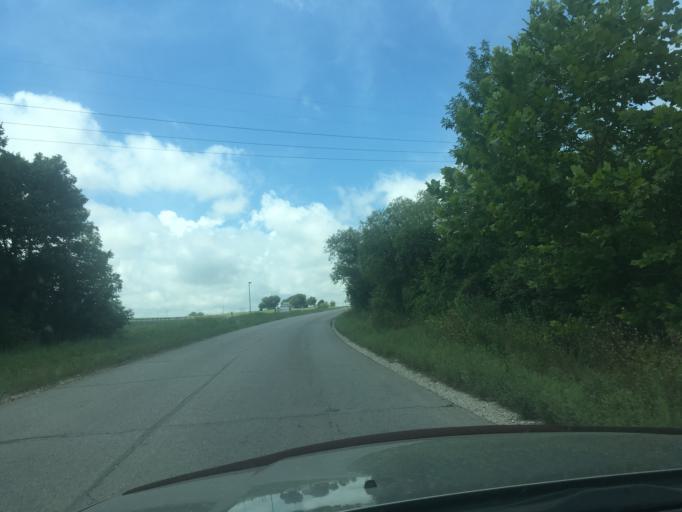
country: US
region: Kansas
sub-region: Atchison County
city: Atchison
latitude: 39.5385
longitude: -95.1264
